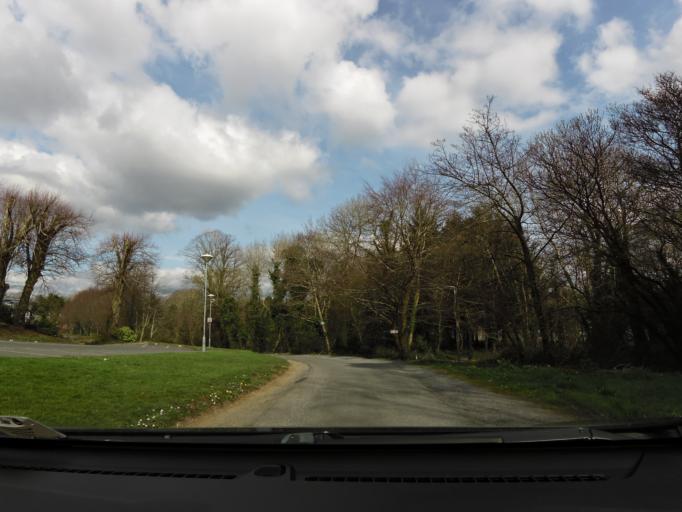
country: IE
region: Connaught
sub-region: County Galway
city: Gaillimh
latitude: 53.2900
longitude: -9.0730
